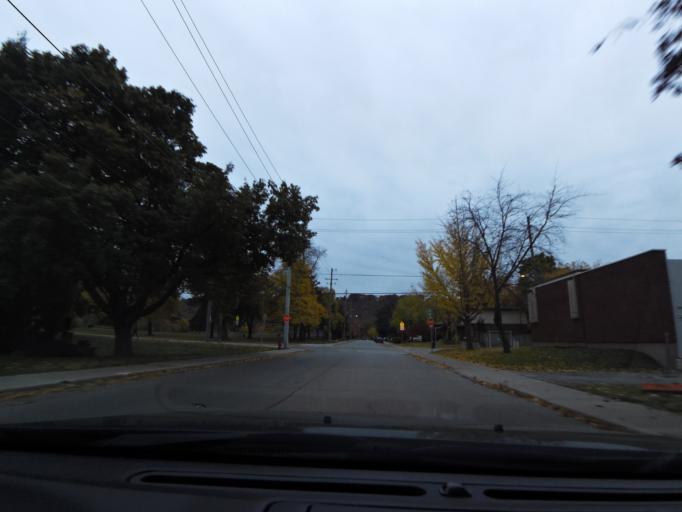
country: CA
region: Ontario
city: Ancaster
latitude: 43.2533
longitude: -79.9292
